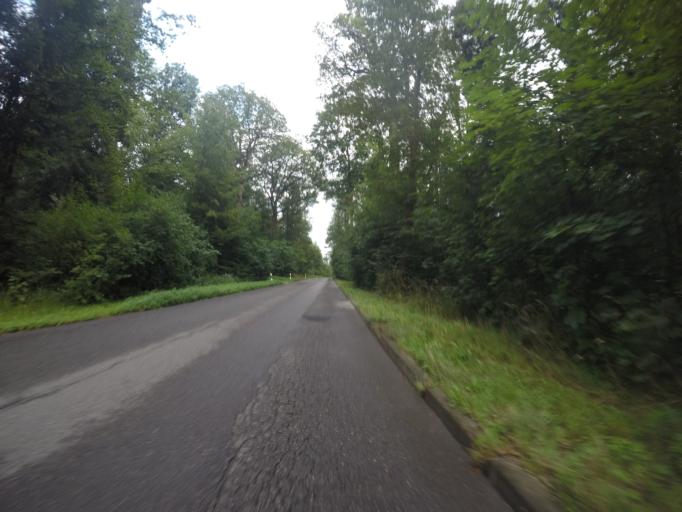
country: DE
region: Baden-Wuerttemberg
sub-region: Regierungsbezirk Stuttgart
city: Stuttgart
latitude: 48.7429
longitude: 9.1936
